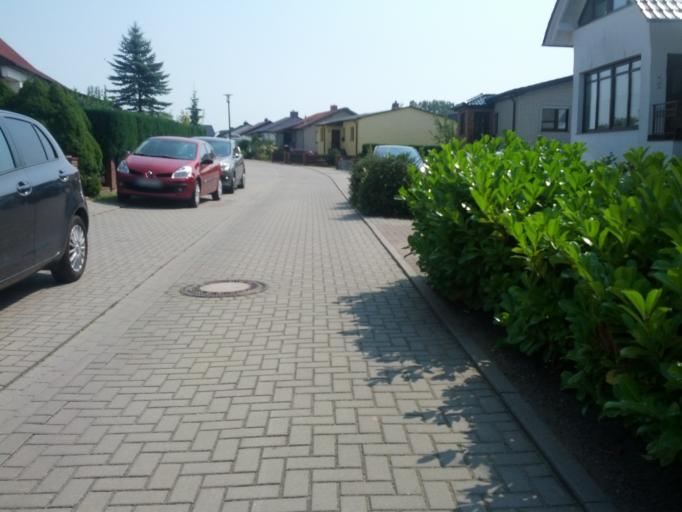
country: DE
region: Mecklenburg-Vorpommern
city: Bastorf
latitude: 54.1018
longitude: 11.6195
